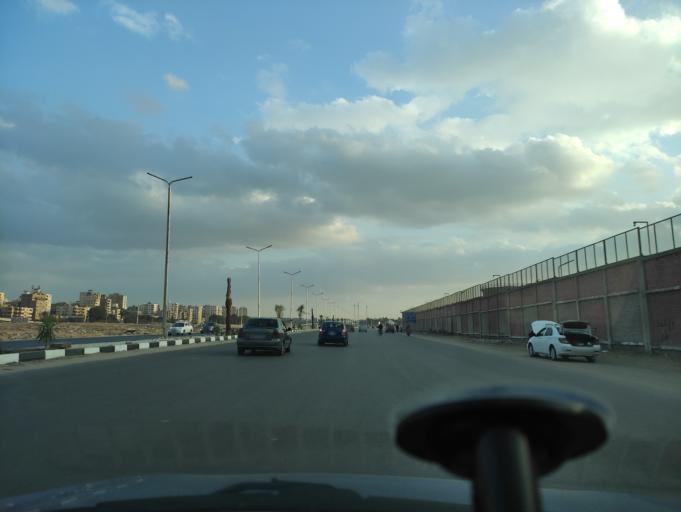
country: EG
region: Muhafazat al Qalyubiyah
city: Al Khankah
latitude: 30.1269
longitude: 31.3599
